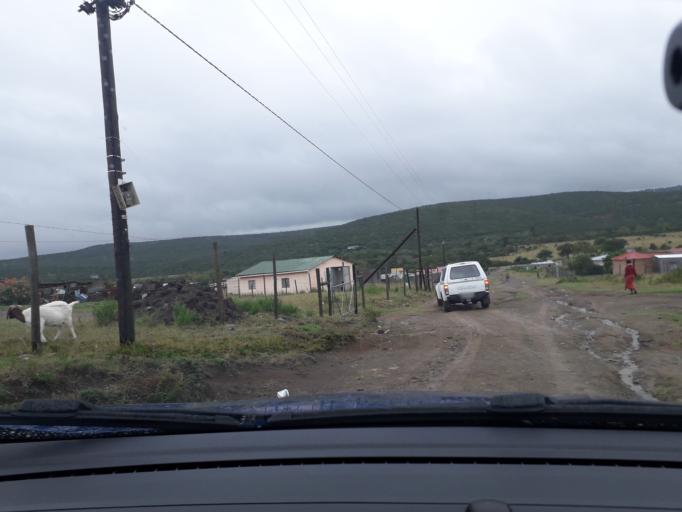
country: ZA
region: Eastern Cape
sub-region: Buffalo City Metropolitan Municipality
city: Bhisho
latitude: -32.8072
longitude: 27.3668
